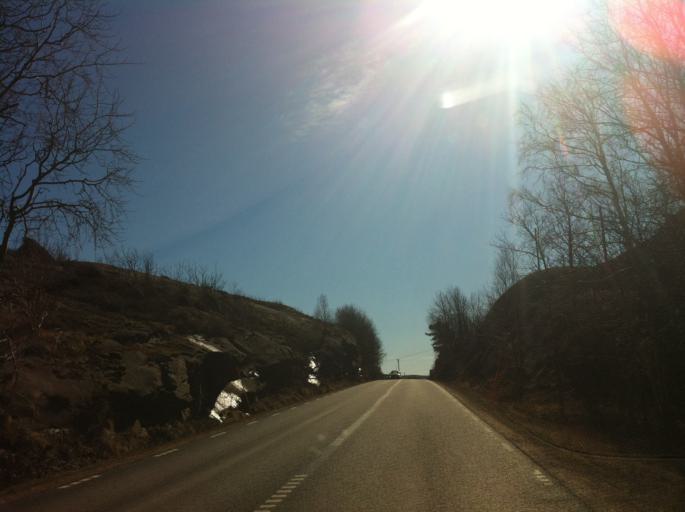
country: SE
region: Vaestra Goetaland
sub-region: Sotenas Kommun
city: Hunnebostrand
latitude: 58.4202
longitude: 11.2942
